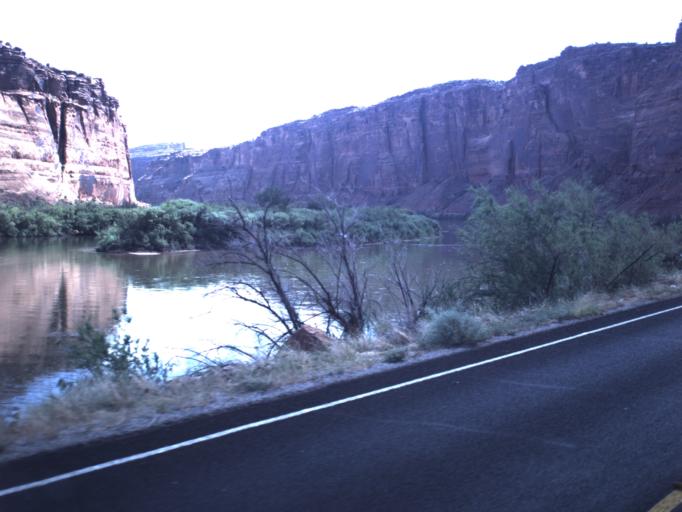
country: US
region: Utah
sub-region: Grand County
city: Moab
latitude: 38.5686
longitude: -109.6575
